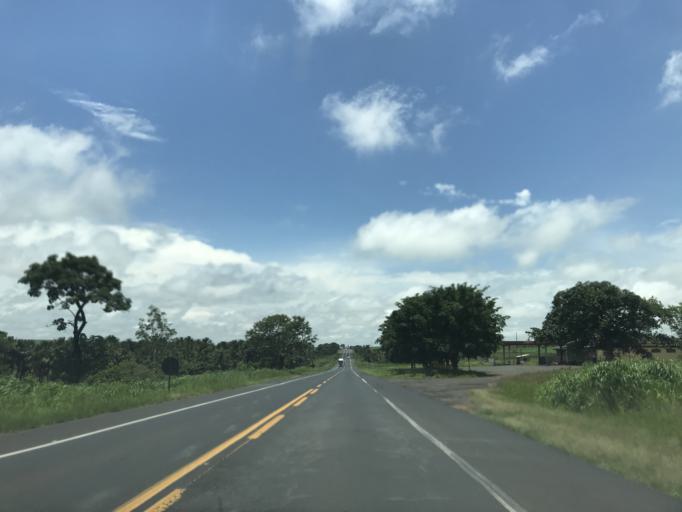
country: BR
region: Minas Gerais
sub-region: Prata
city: Prata
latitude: -19.6371
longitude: -48.8540
